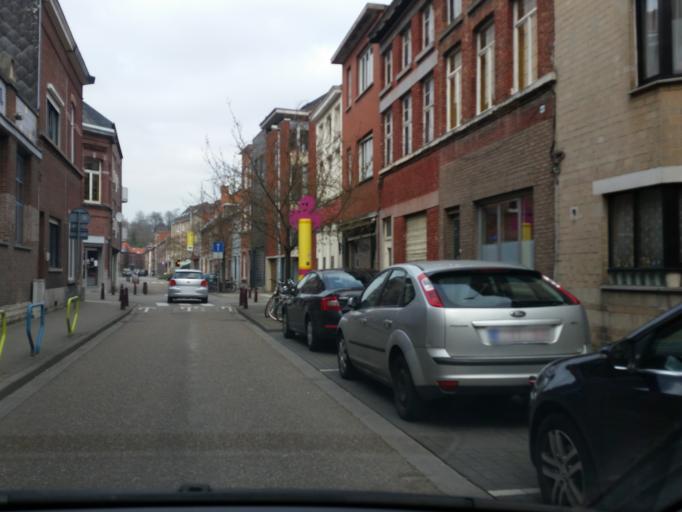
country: BE
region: Flanders
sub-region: Provincie Vlaams-Brabant
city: Leuven
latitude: 50.8830
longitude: 4.6917
